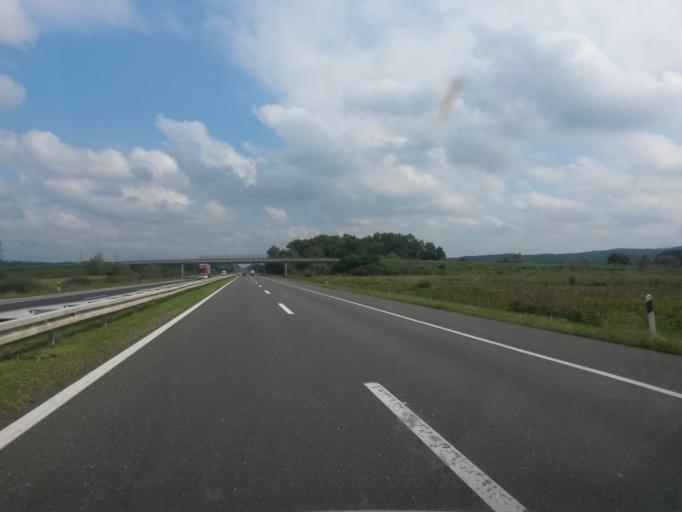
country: HR
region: Zagrebacka
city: Brckovljani
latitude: 45.8804
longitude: 16.2193
